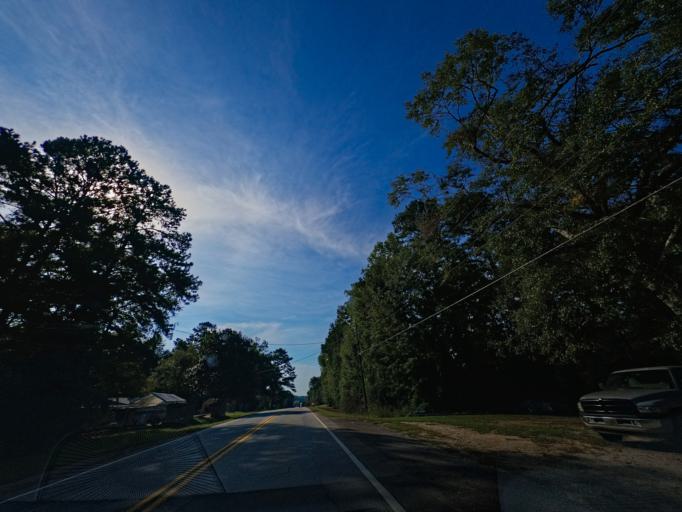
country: US
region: Georgia
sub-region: Troup County
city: Hogansville
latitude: 33.1963
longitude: -84.9210
